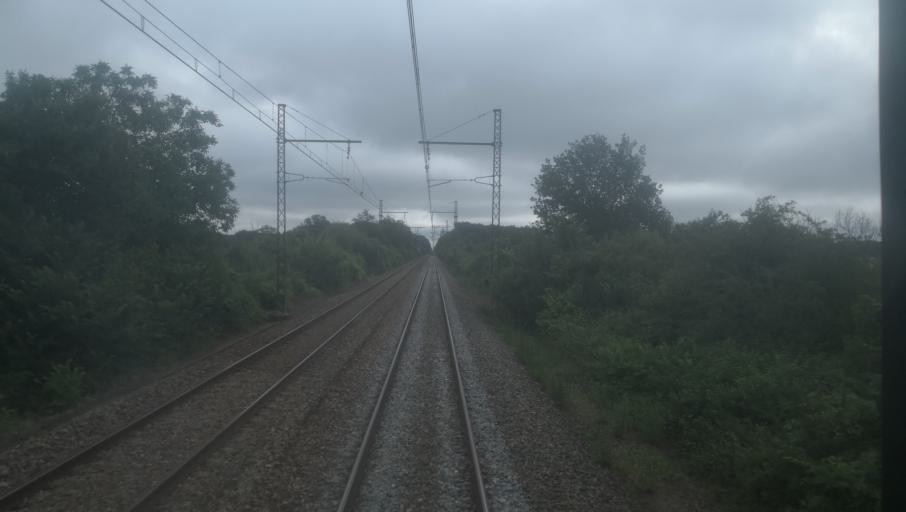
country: FR
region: Centre
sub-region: Departement de l'Indre
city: Montierchaume
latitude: 46.8447
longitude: 1.7802
